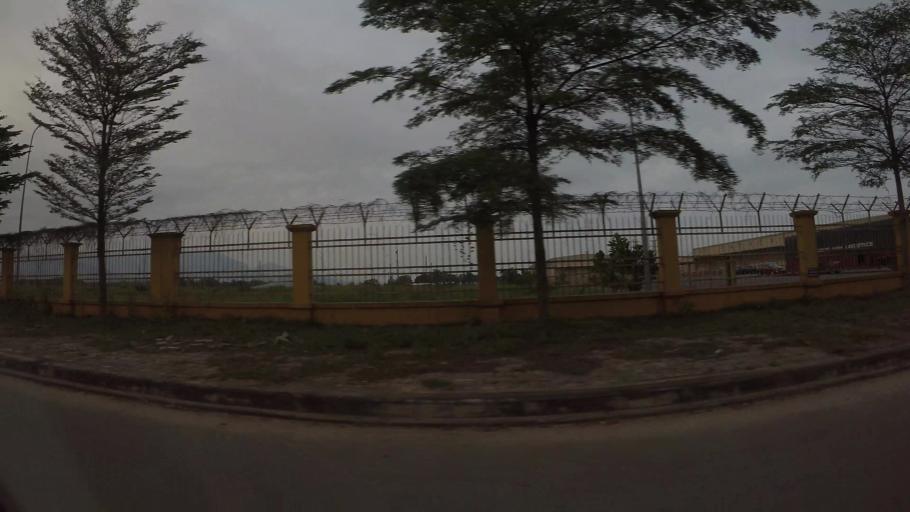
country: VN
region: Da Nang
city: Lien Chieu
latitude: 16.0862
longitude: 108.1136
